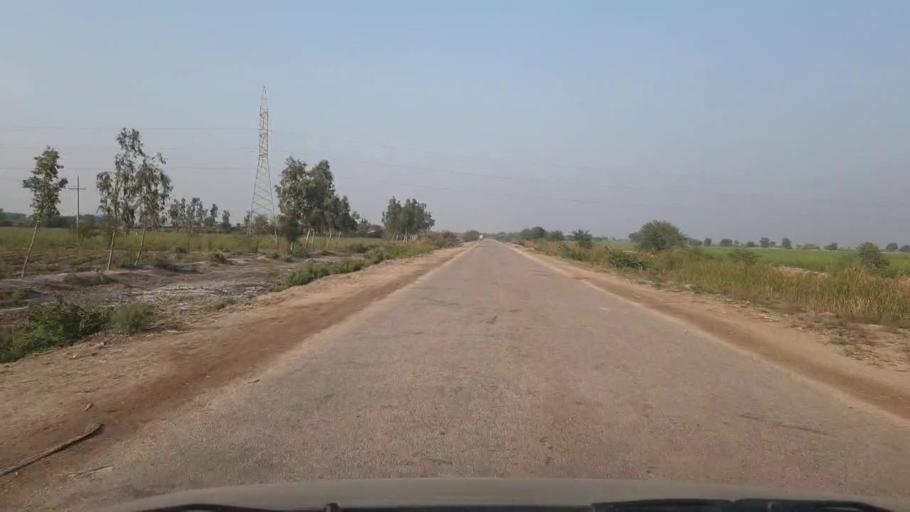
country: PK
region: Sindh
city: Mirwah Gorchani
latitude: 25.3172
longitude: 69.1648
